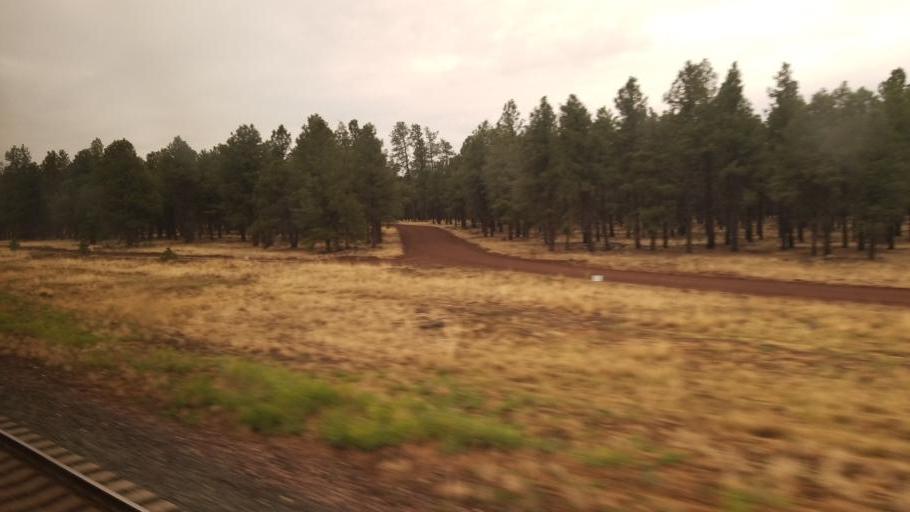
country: US
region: Arizona
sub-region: Coconino County
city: Flagstaff
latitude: 35.2160
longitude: -111.7877
